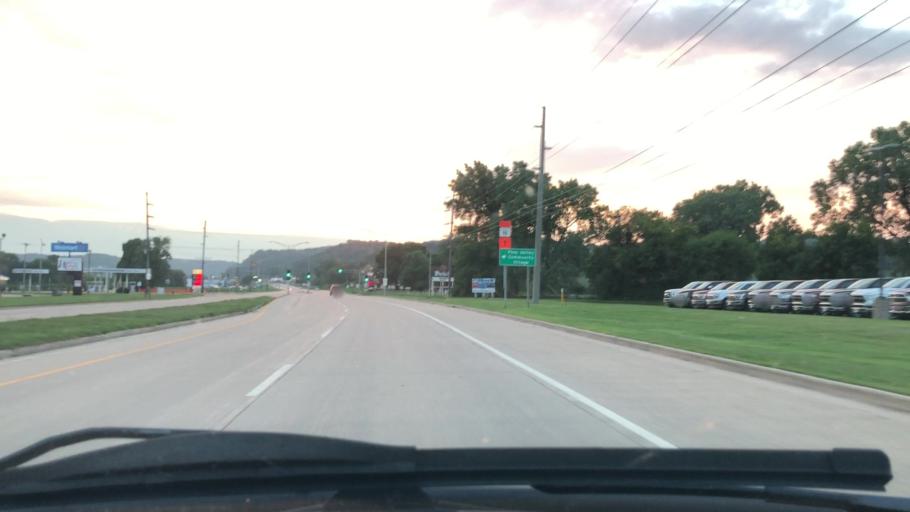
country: US
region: Wisconsin
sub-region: Richland County
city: Richland Center
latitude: 43.3146
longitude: -90.3485
